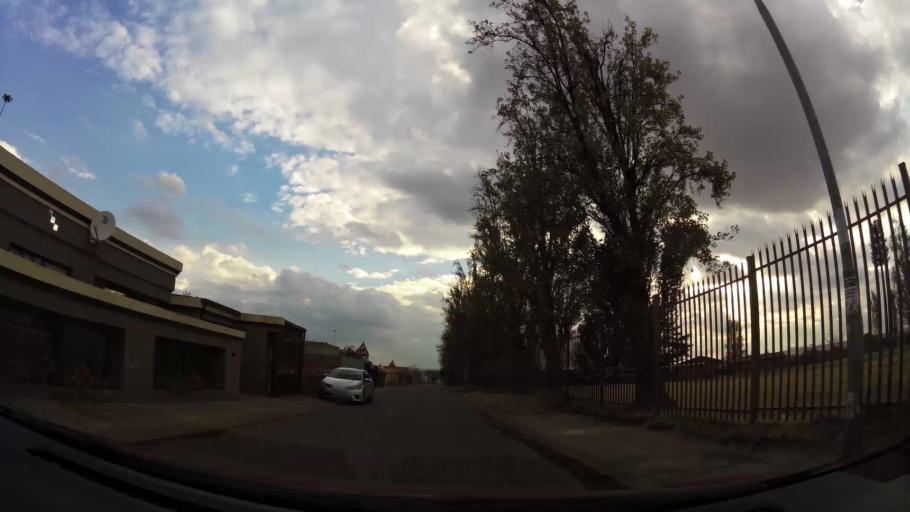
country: ZA
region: Gauteng
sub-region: City of Johannesburg Metropolitan Municipality
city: Soweto
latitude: -26.2422
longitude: 27.8245
